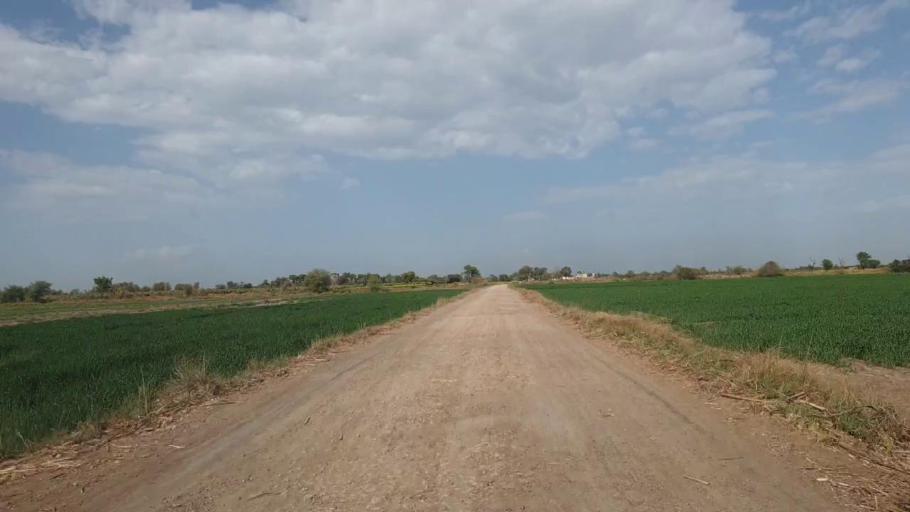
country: PK
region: Sindh
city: Shahdadpur
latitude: 25.9782
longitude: 68.4770
